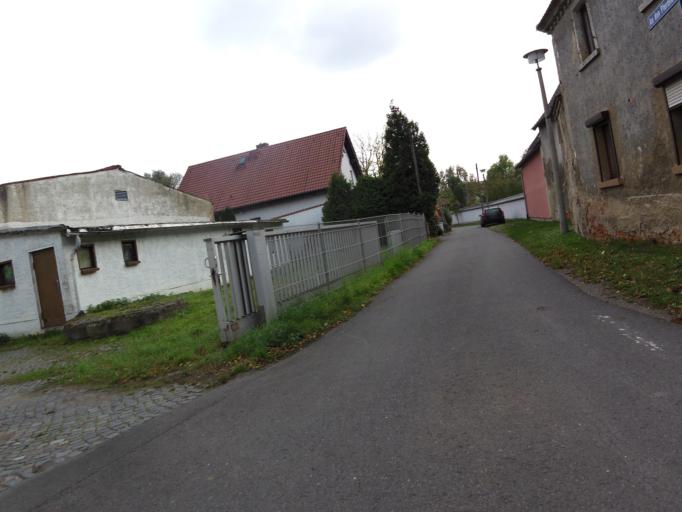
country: DE
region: Saxony
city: Taucha
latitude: 51.3822
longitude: 12.4356
